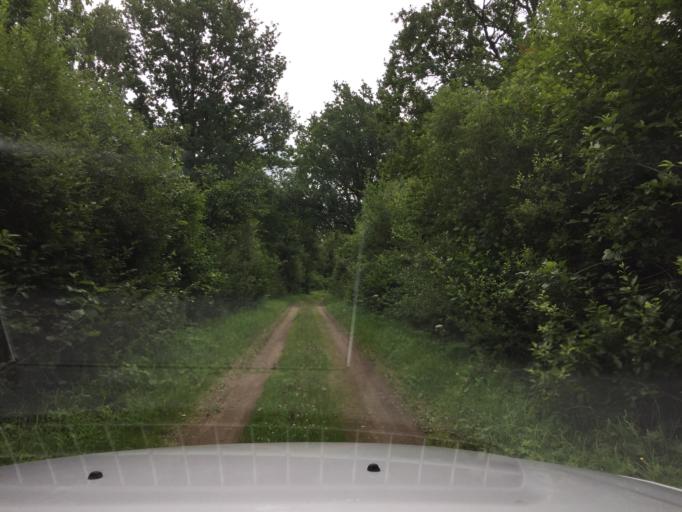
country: SE
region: Skane
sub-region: Hassleholms Kommun
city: Sosdala
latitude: 56.0275
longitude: 13.7003
